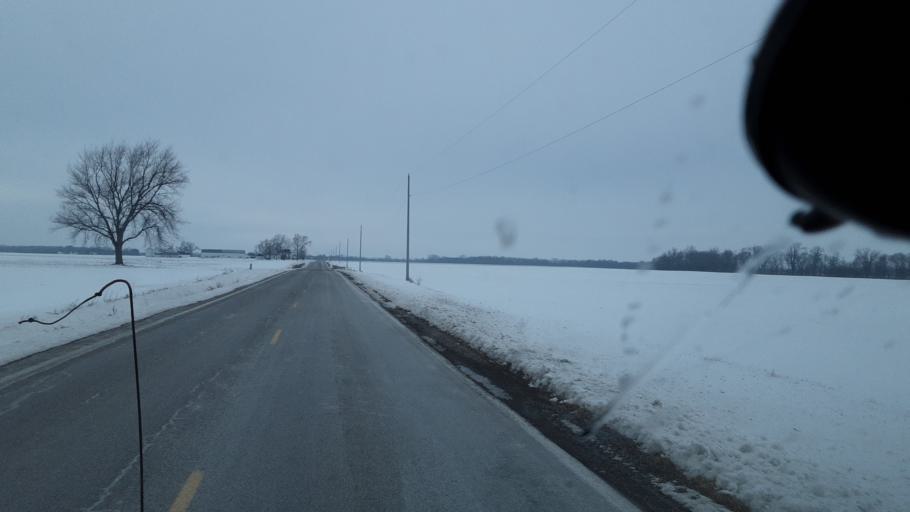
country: US
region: Ohio
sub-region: Champaign County
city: Mechanicsburg
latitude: 40.1169
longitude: -83.4302
